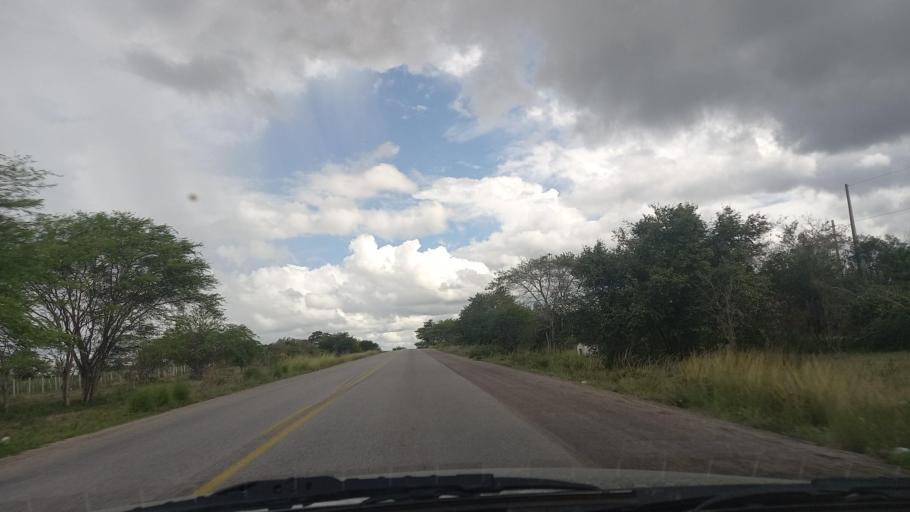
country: BR
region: Pernambuco
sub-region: Cachoeirinha
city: Cachoeirinha
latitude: -8.5339
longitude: -36.2653
